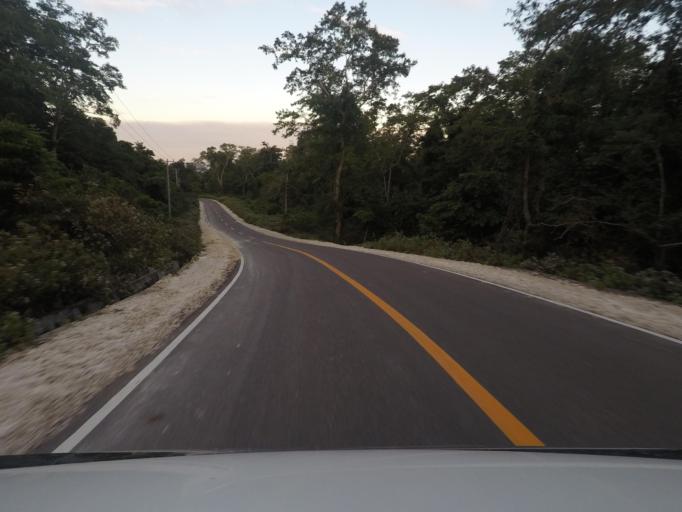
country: TL
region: Lautem
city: Lospalos
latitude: -8.4031
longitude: 127.2854
